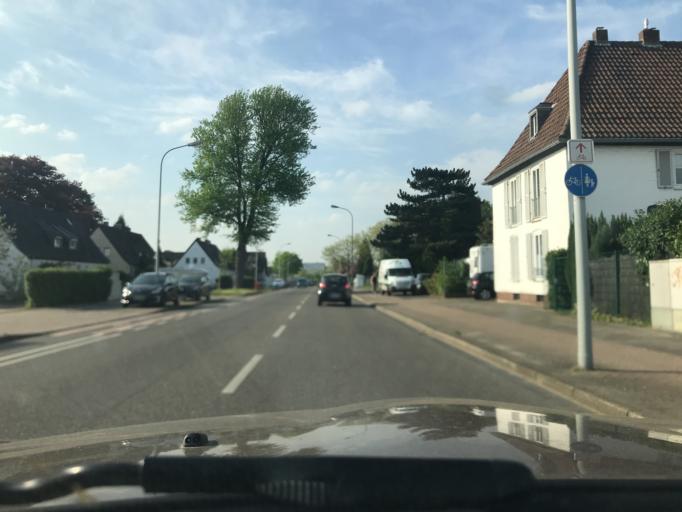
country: DE
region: North Rhine-Westphalia
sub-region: Regierungsbezirk Dusseldorf
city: Krefeld
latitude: 51.3118
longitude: 6.5699
